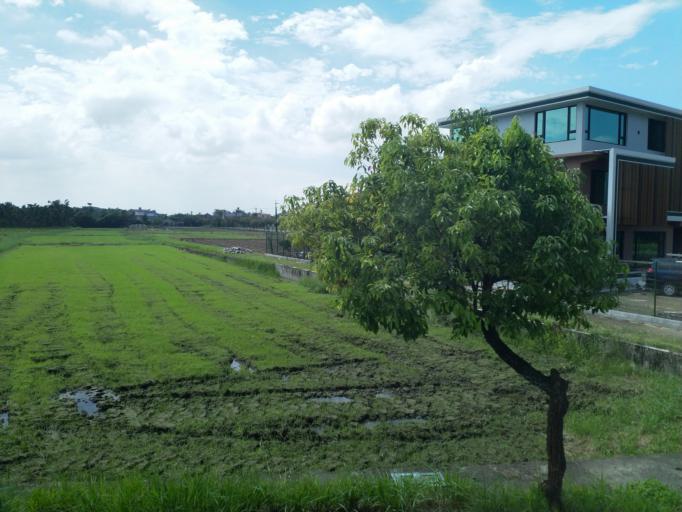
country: TW
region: Taiwan
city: Yujing
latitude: 22.9045
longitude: 120.5513
